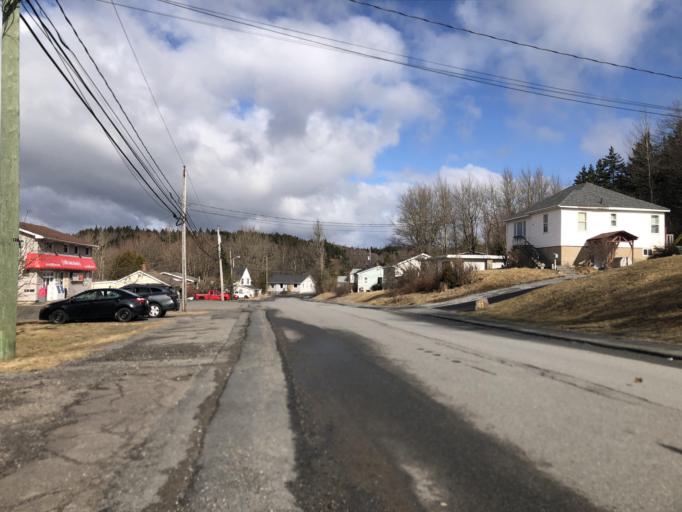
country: CA
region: New Brunswick
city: Saint John
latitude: 45.3208
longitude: -66.0103
